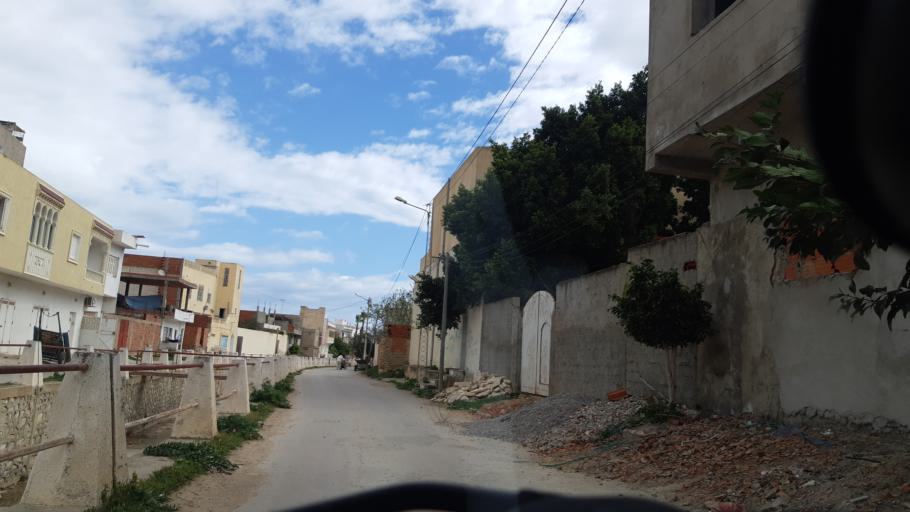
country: TN
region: Susah
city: Akouda
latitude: 35.8669
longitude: 10.5344
